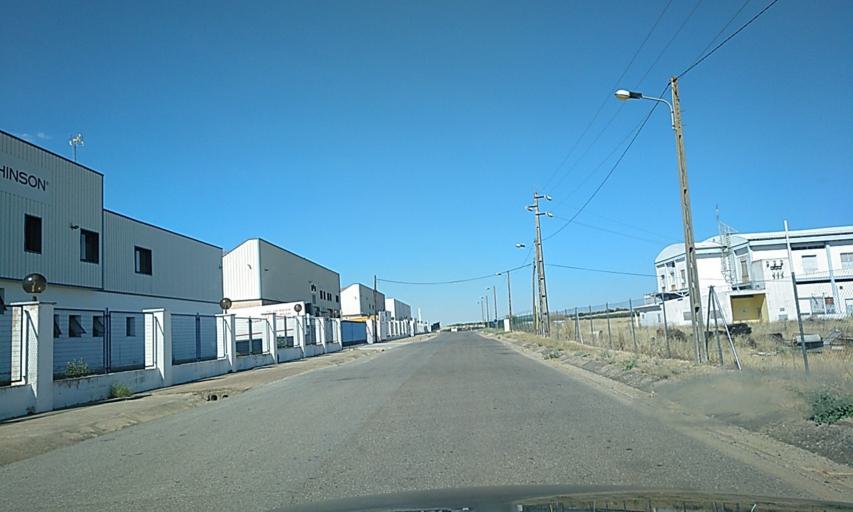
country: PT
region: Portalegre
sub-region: Campo Maior
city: Campo Maior
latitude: 39.0238
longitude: -7.0608
